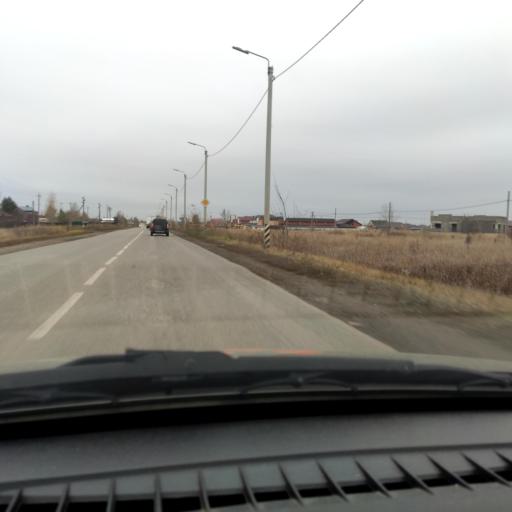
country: RU
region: Samara
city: Podstepki
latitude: 53.5224
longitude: 49.1666
